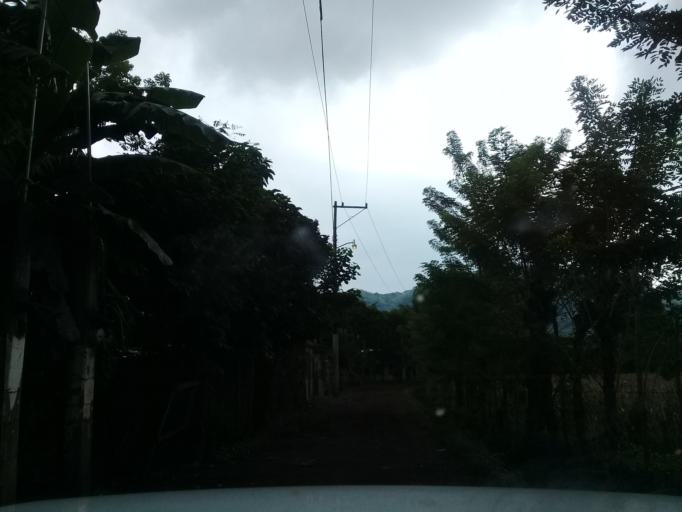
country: MX
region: Veracruz
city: Comoapan
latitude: 18.4016
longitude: -95.1723
